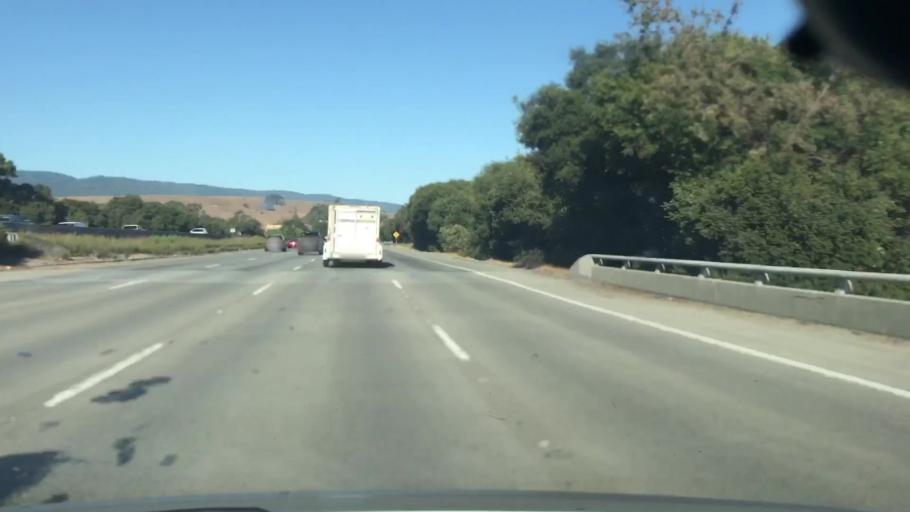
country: US
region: California
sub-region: San Mateo County
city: Ladera
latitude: 37.4094
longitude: -122.1948
